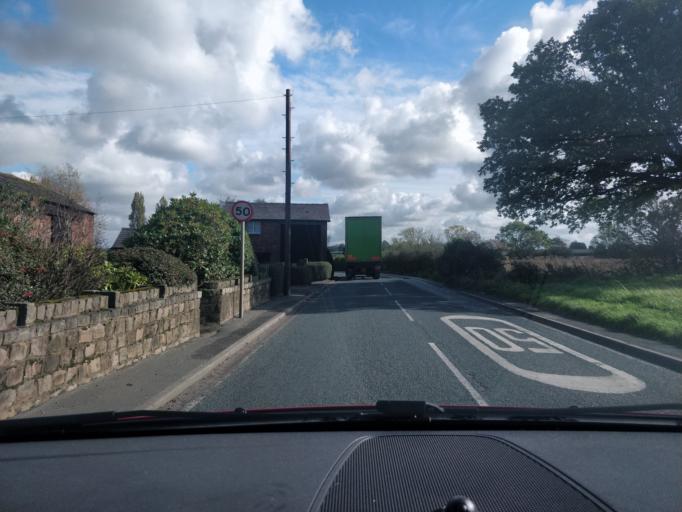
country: GB
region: England
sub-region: Lancashire
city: Ormskirk
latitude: 53.5900
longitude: -2.8790
